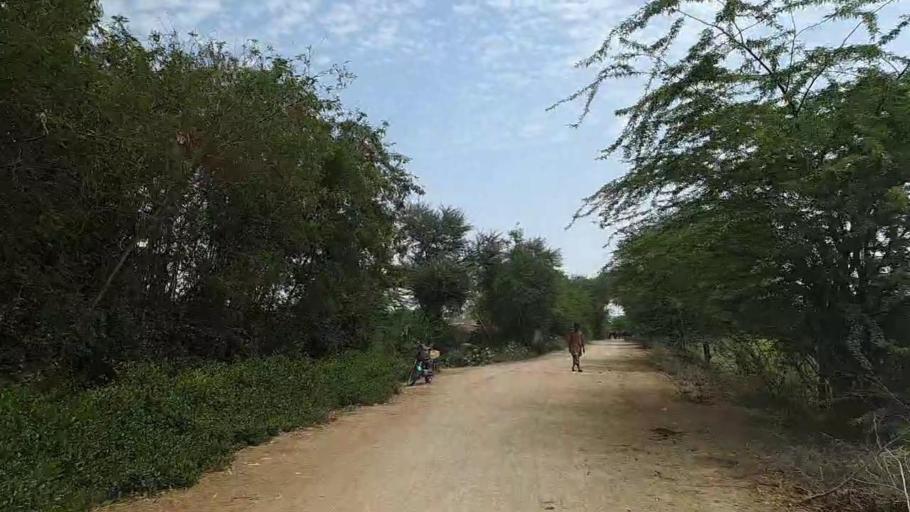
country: PK
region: Sindh
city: Daro Mehar
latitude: 24.7799
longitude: 68.2209
